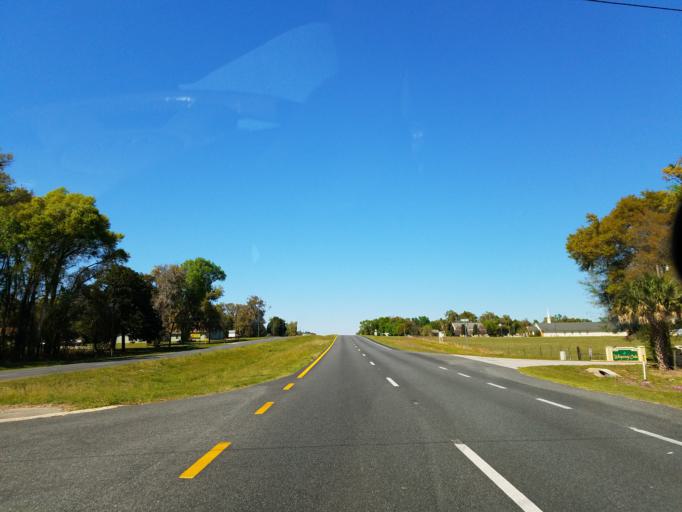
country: US
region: Florida
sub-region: Marion County
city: Belleview
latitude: 29.0400
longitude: -82.0451
